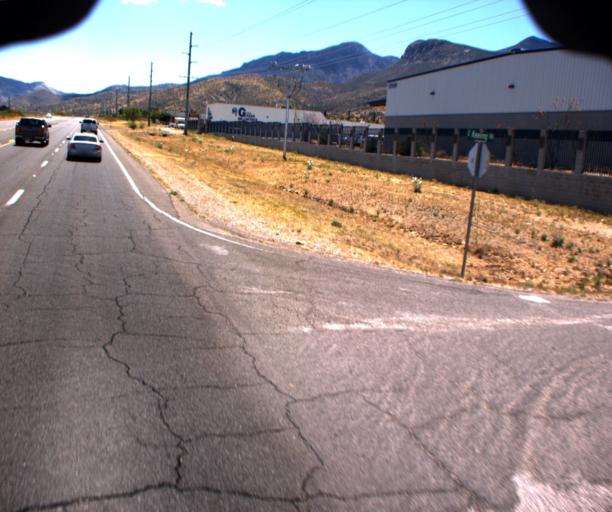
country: US
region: Arizona
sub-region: Cochise County
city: Sierra Vista Southeast
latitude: 31.4624
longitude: -110.2575
